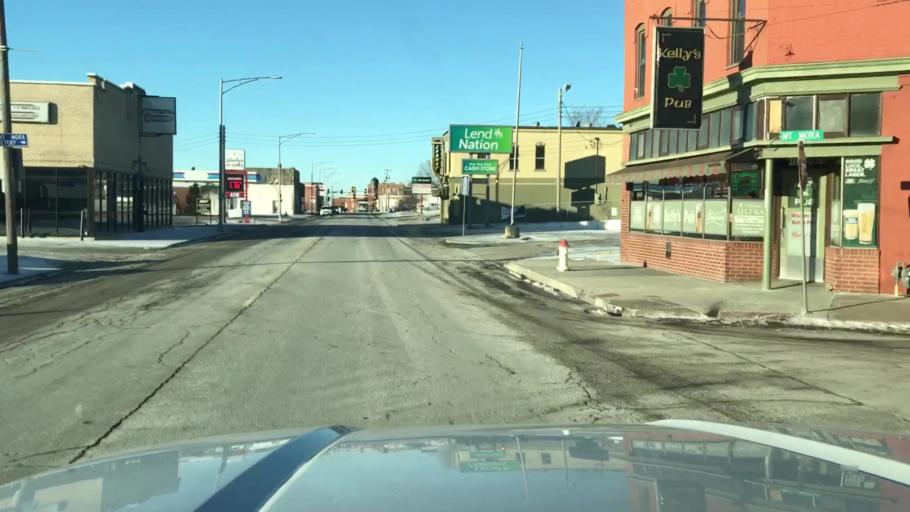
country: US
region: Missouri
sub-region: Buchanan County
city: Saint Joseph
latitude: 39.7717
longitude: -94.8419
